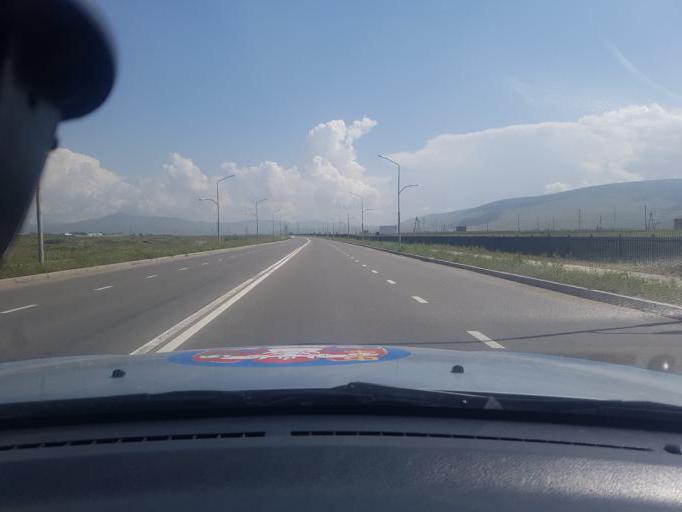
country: MN
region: Ulaanbaatar
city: Ulaanbaatar
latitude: 47.9020
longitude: 106.9843
